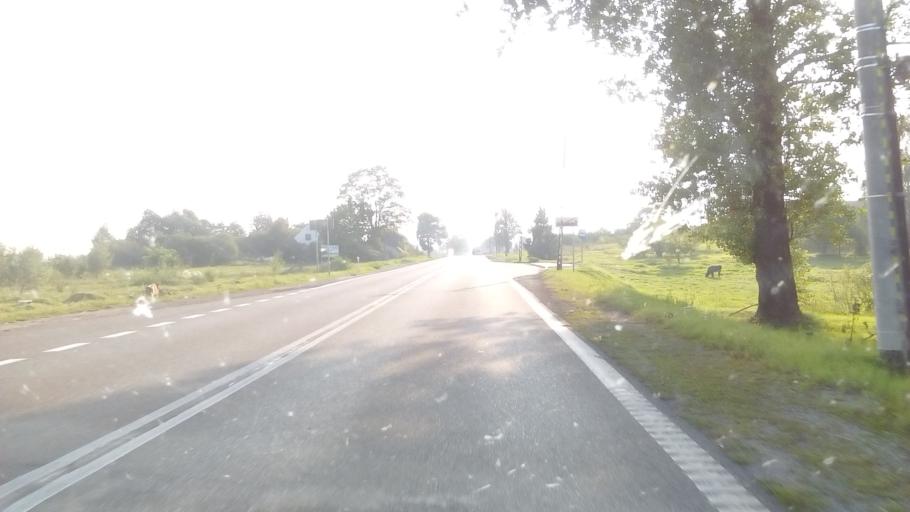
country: PL
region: Podlasie
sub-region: Powiat augustowski
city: Augustow
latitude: 53.8296
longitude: 22.9551
